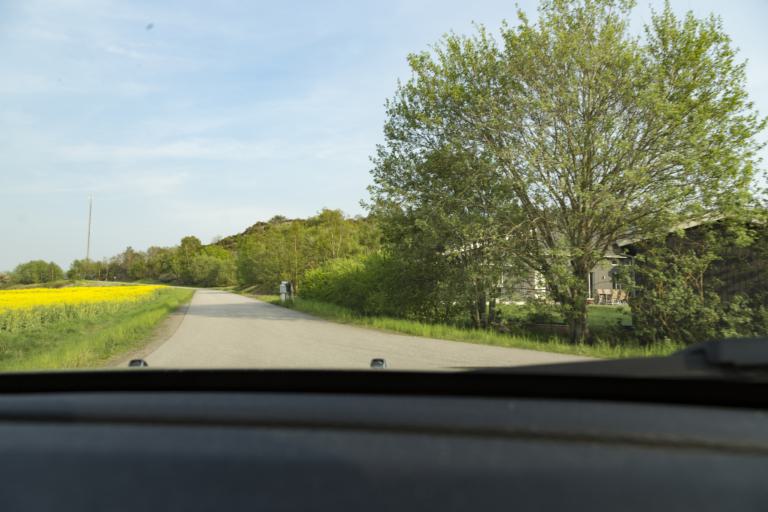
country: SE
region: Halland
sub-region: Varbergs Kommun
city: Varberg
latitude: 57.1571
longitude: 12.2411
